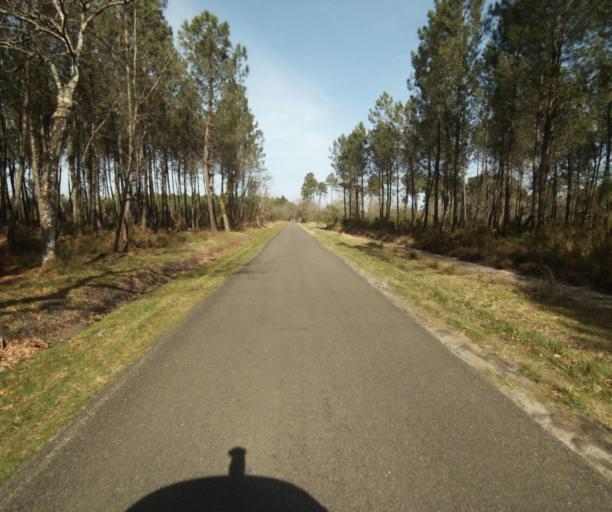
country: FR
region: Aquitaine
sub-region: Departement de la Gironde
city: Bazas
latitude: 44.2399
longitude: -0.1996
